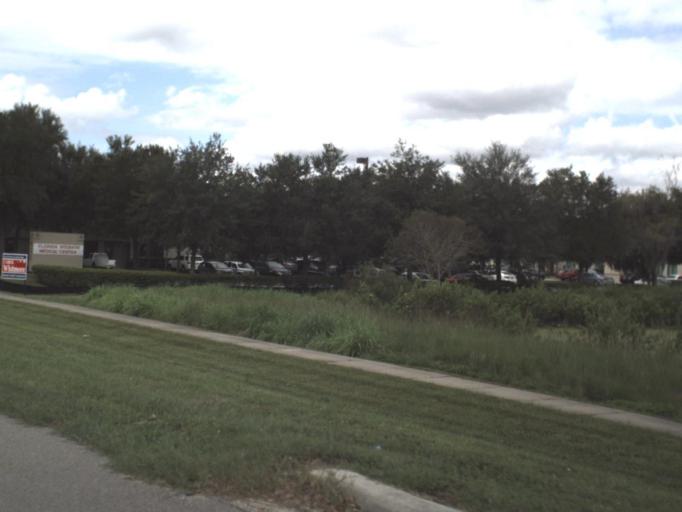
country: US
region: Florida
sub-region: Sarasota County
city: North Sarasota
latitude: 27.3891
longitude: -82.5202
